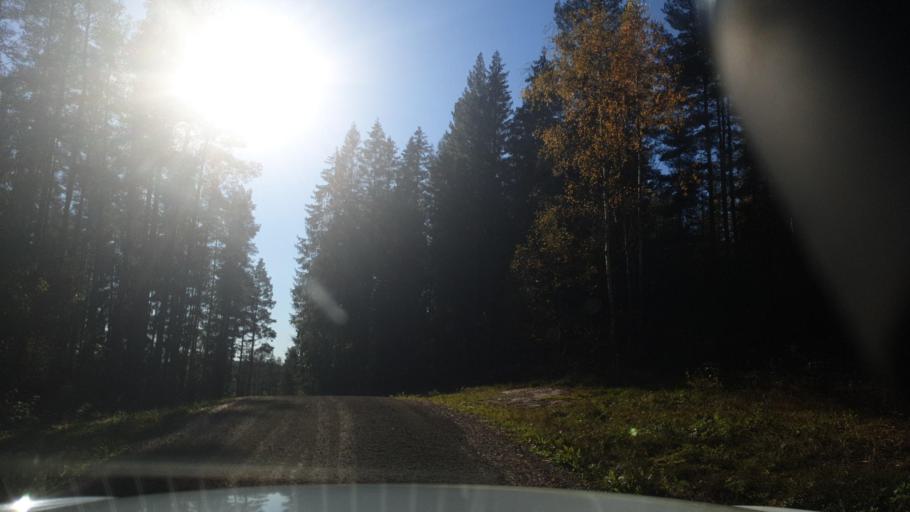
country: SE
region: Vaermland
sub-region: Grums Kommun
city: Grums
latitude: 59.4953
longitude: 12.9272
